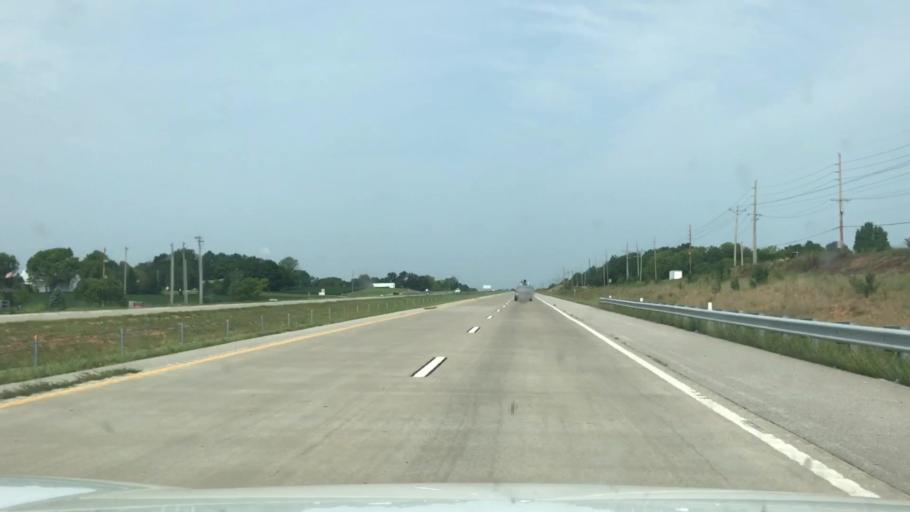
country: US
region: Missouri
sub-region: Saint Charles County
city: Dardenne Prairie
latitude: 38.7611
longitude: -90.7190
